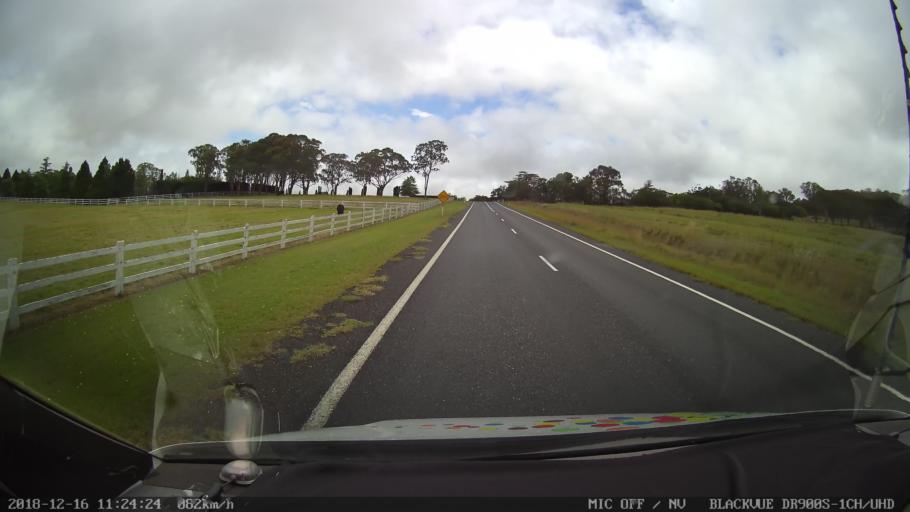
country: AU
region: New South Wales
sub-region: Tenterfield Municipality
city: Carrolls Creek
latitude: -29.0579
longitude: 152.0475
